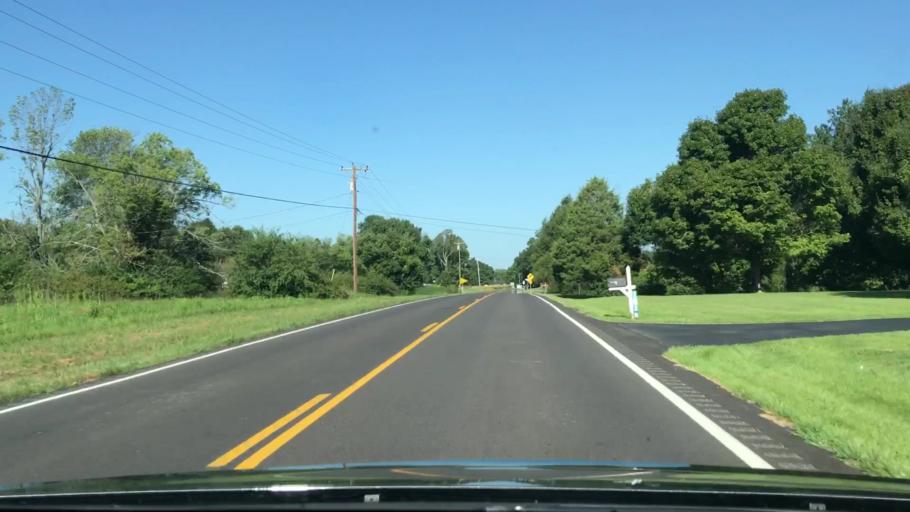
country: US
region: Kentucky
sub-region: Marshall County
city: Benton
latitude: 36.7677
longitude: -88.4335
